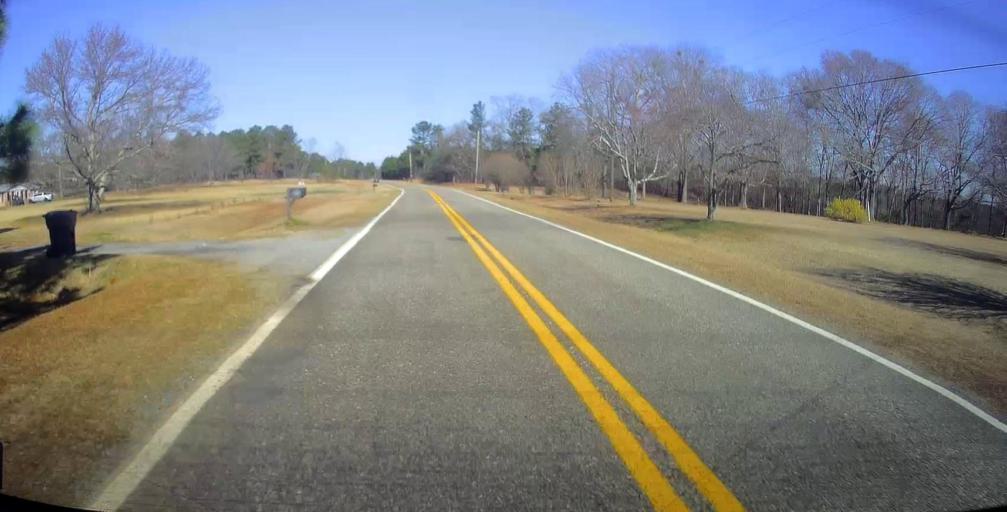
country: US
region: Georgia
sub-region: Peach County
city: Fort Valley
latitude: 32.6331
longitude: -83.9402
